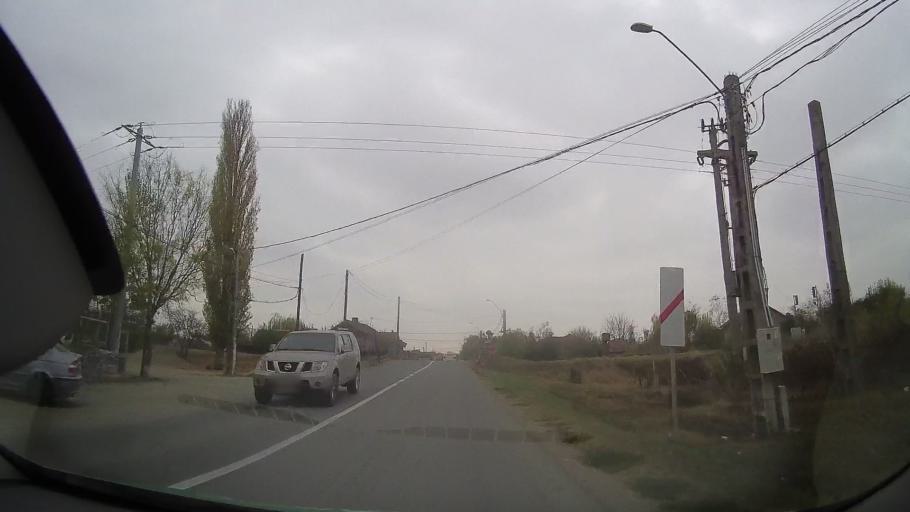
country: RO
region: Ialomita
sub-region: Comuna Manasia
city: Manasia
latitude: 44.7085
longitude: 26.6726
